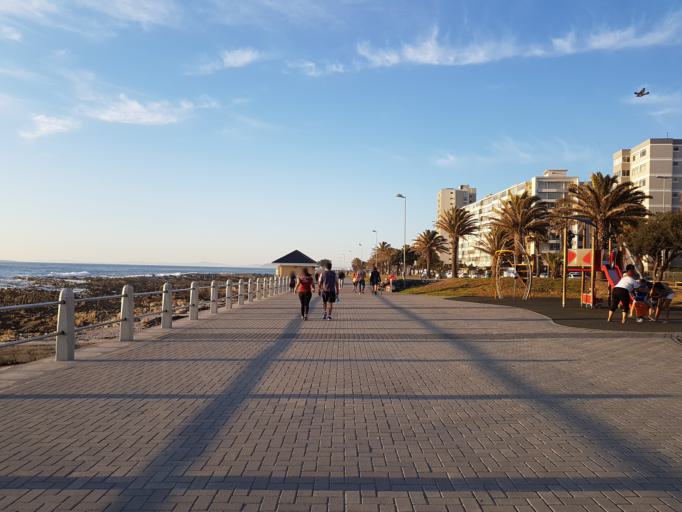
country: ZA
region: Western Cape
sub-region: City of Cape Town
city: Cape Town
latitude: -33.9143
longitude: 18.3871
